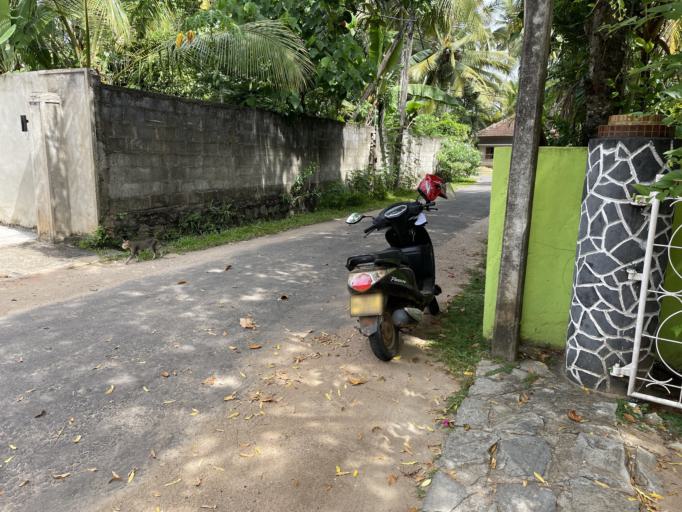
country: LK
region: North Western
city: Kurunegala
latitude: 7.4993
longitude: 80.3461
